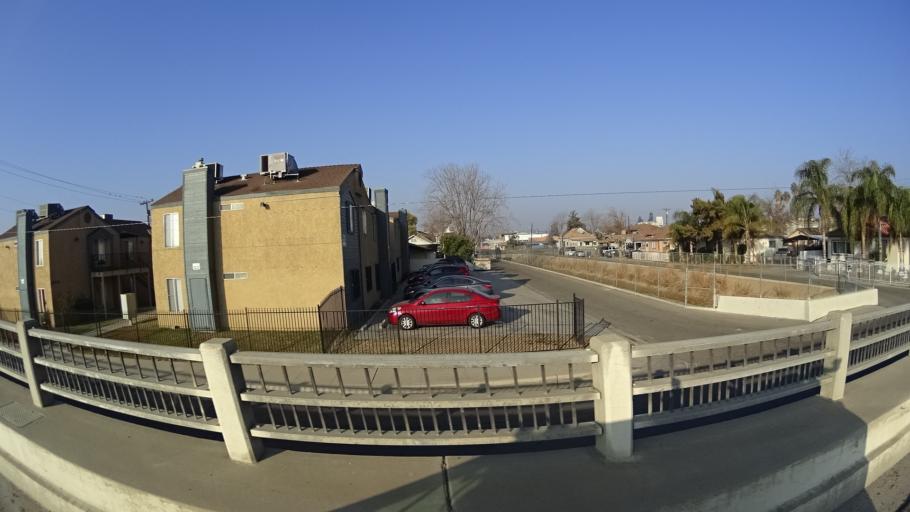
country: US
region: California
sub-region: Kern County
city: Bakersfield
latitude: 35.3789
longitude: -118.9888
